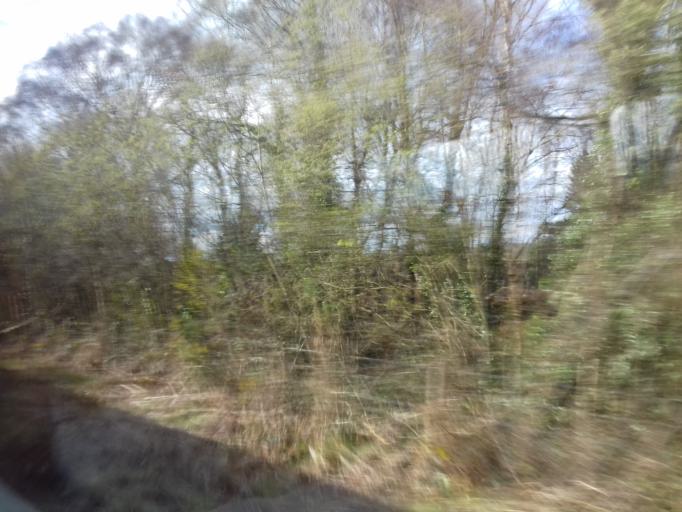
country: IE
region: Leinster
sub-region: An Iarmhi
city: Kinnegad
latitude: 53.4762
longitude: -7.0425
